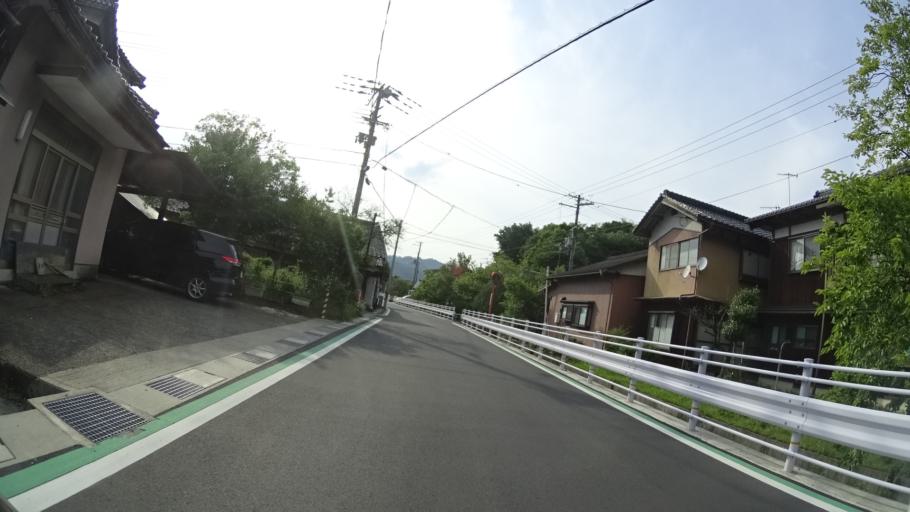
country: JP
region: Kyoto
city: Miyazu
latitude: 35.5300
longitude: 135.1267
